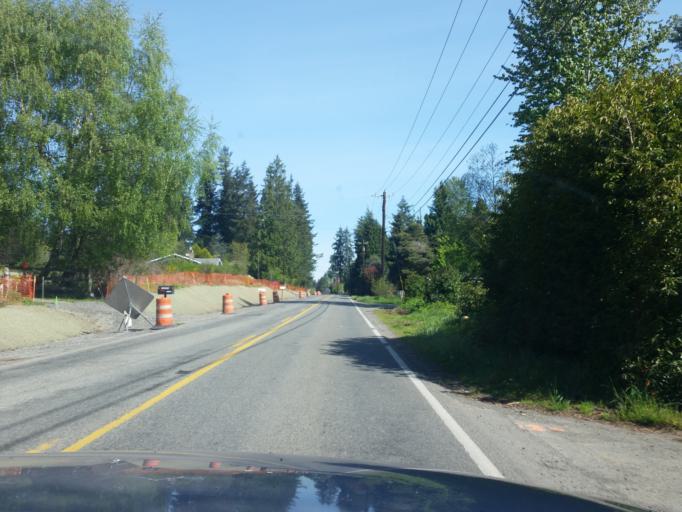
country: US
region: Washington
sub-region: Snohomish County
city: Maltby
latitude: 47.8208
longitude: -122.1098
